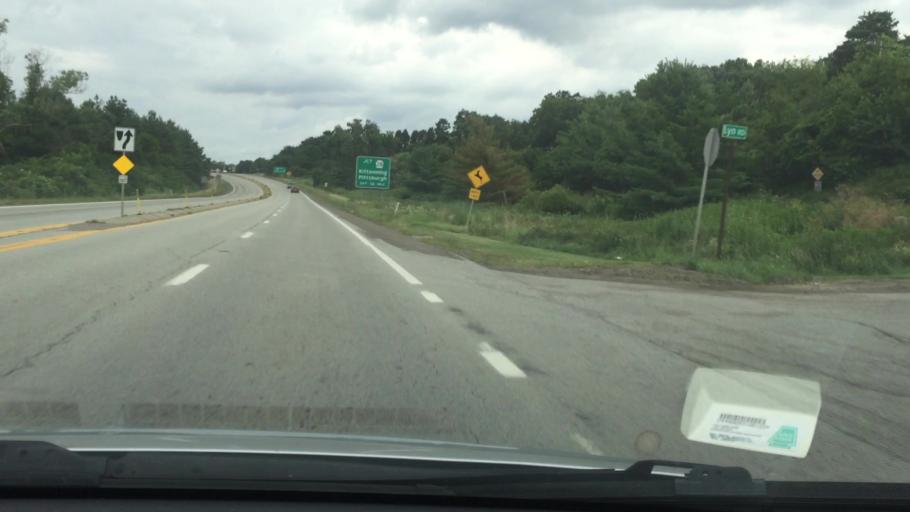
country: US
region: Pennsylvania
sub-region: Armstrong County
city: Freeport
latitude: 40.6875
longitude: -79.7027
